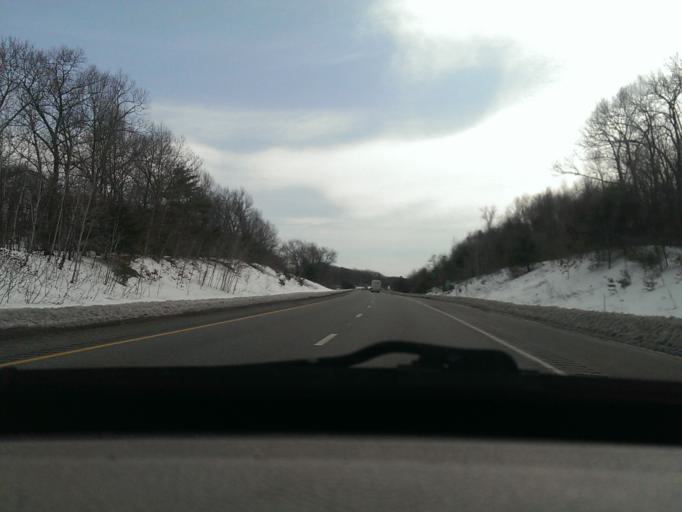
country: US
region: Massachusetts
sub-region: Worcester County
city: Whitinsville
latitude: 42.1196
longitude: -71.7070
